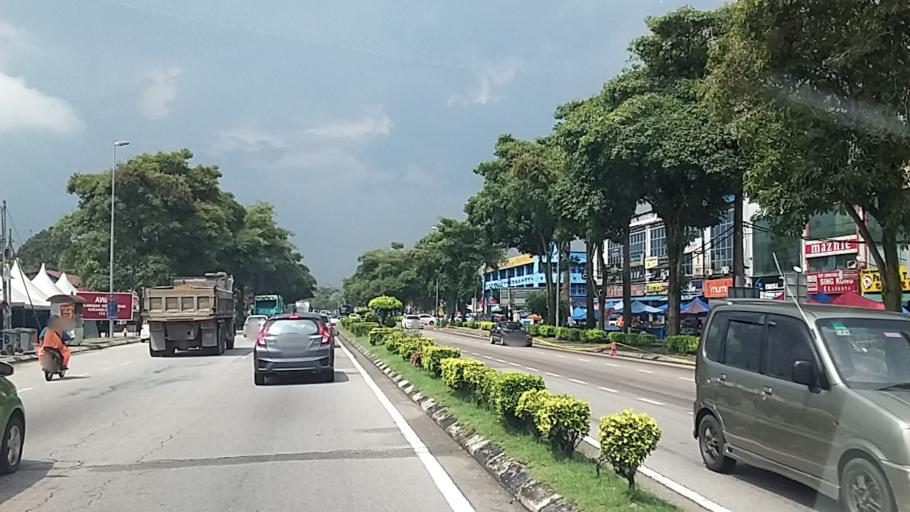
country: MY
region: Johor
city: Parit Raja
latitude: 1.8656
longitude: 103.1129
